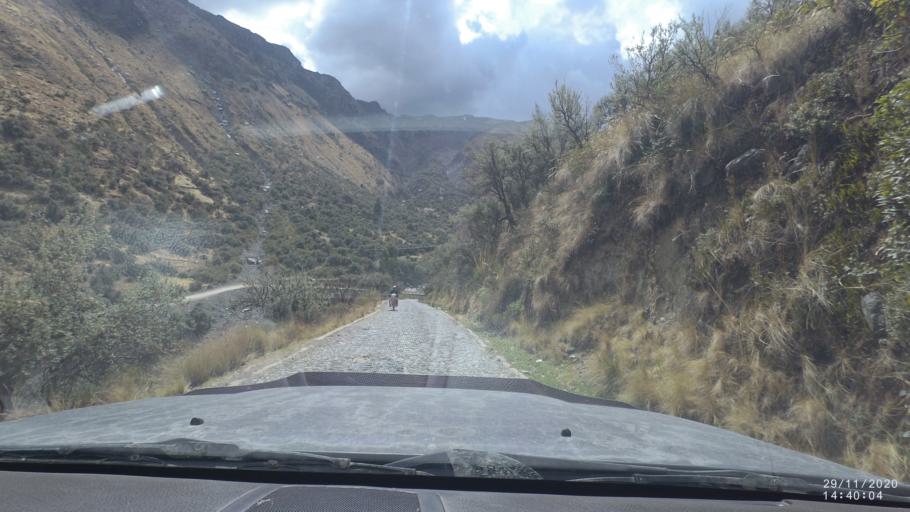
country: BO
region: Cochabamba
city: Sipe Sipe
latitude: -17.2747
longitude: -66.3287
